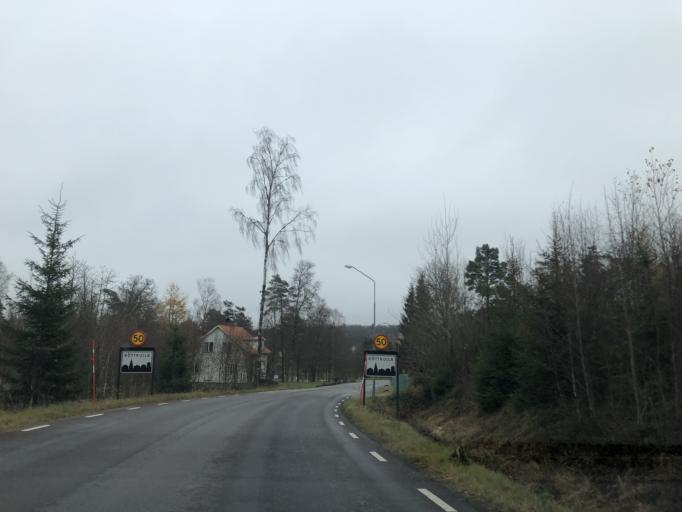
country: SE
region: Vaestra Goetaland
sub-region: Ulricehamns Kommun
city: Ulricehamn
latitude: 57.6982
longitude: 13.5711
